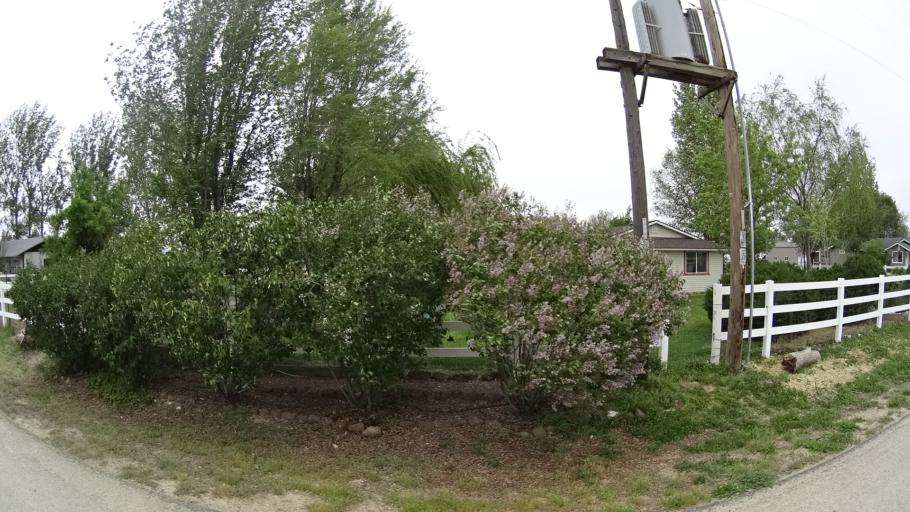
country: US
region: Idaho
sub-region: Ada County
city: Kuna
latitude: 43.4818
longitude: -116.3143
